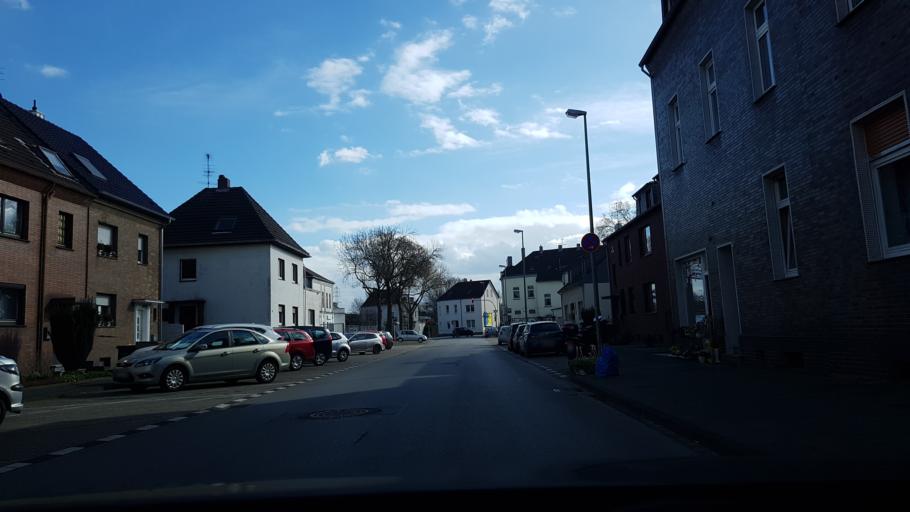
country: DE
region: North Rhine-Westphalia
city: Meiderich
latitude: 51.5104
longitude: 6.7904
